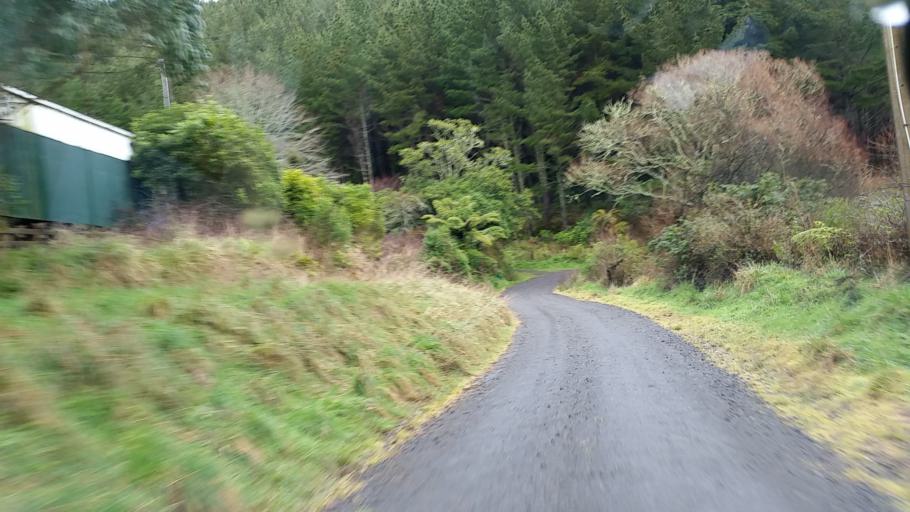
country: NZ
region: Taranaki
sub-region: South Taranaki District
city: Eltham
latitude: -39.5020
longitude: 174.4189
